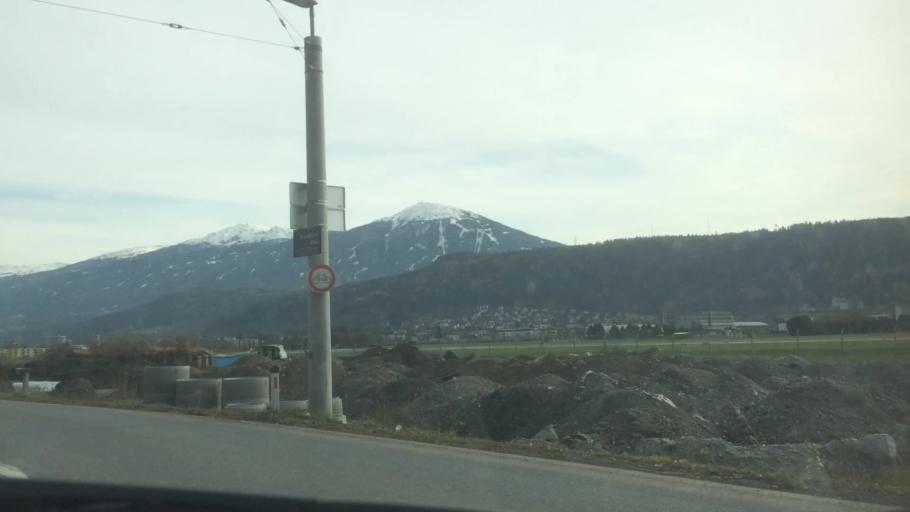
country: AT
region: Tyrol
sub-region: Politischer Bezirk Innsbruck Land
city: Vols
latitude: 47.2630
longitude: 11.3521
